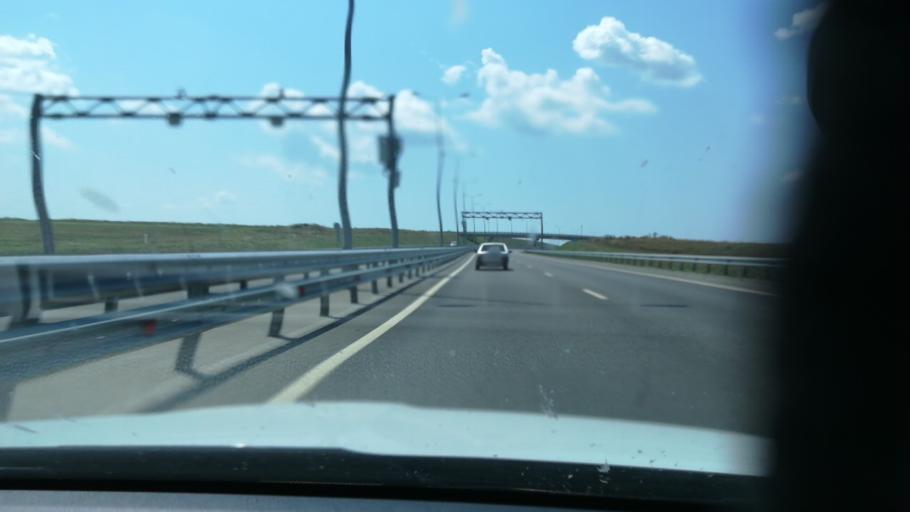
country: RU
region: Krasnodarskiy
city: Vyshestebliyevskaya
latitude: 45.2394
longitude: 37.0535
